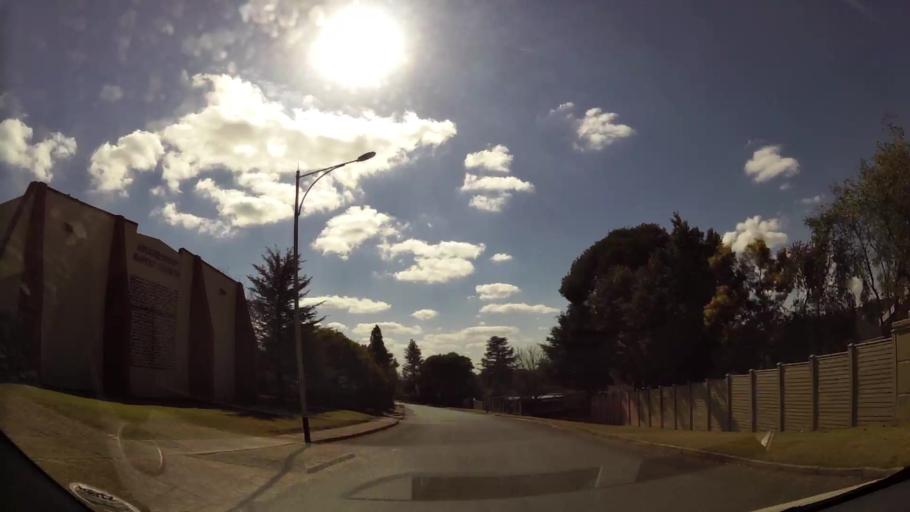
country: ZA
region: Gauteng
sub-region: West Rand District Municipality
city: Krugersdorp
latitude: -26.0974
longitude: 27.7970
